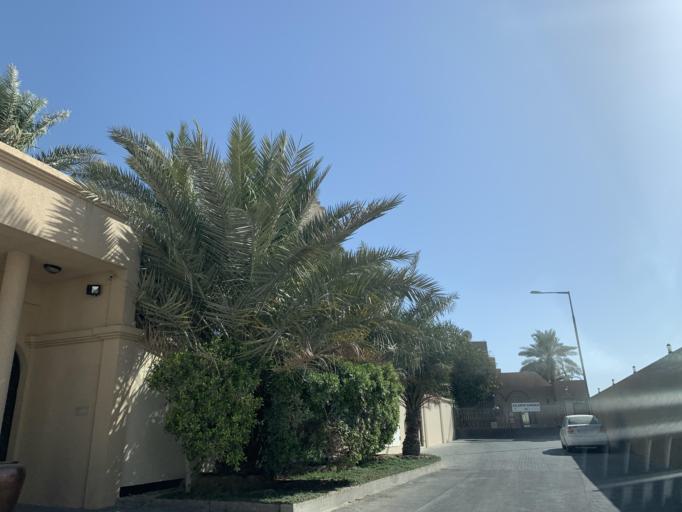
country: BH
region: Manama
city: Jidd Hafs
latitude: 26.2052
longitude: 50.4505
